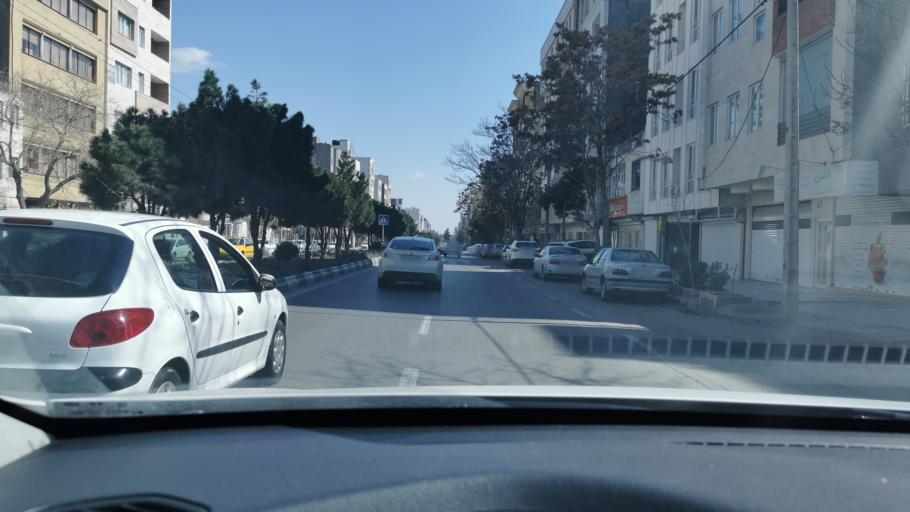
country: IR
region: Razavi Khorasan
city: Mashhad
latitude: 36.3258
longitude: 59.5219
